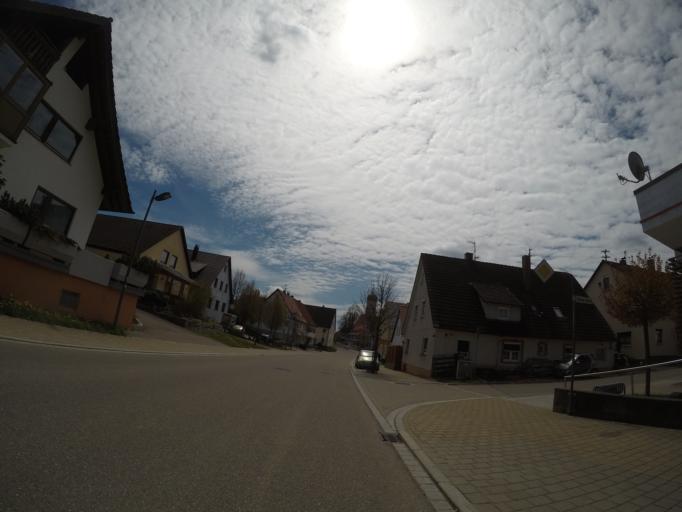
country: DE
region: Baden-Wuerttemberg
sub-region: Tuebingen Region
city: Westerheim
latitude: 48.5159
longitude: 9.6244
